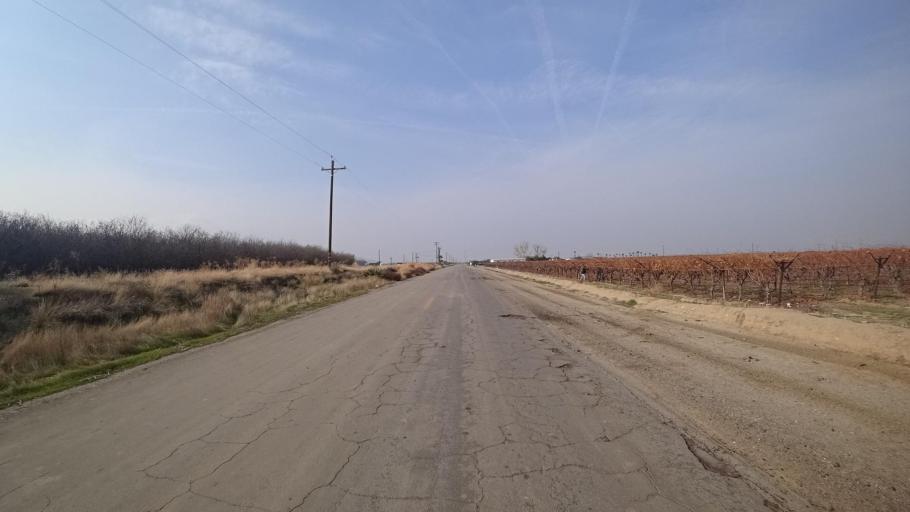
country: US
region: California
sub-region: Kern County
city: Lebec
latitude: 35.0324
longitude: -118.9462
